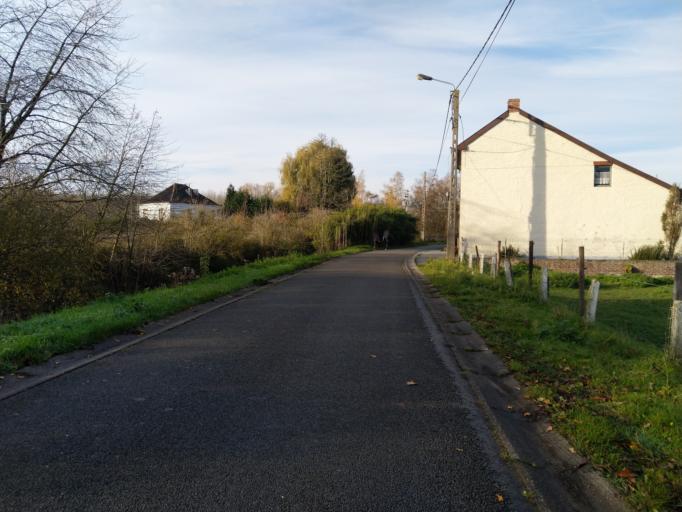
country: BE
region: Wallonia
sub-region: Province du Hainaut
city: Boussu
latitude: 50.4395
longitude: 3.7814
